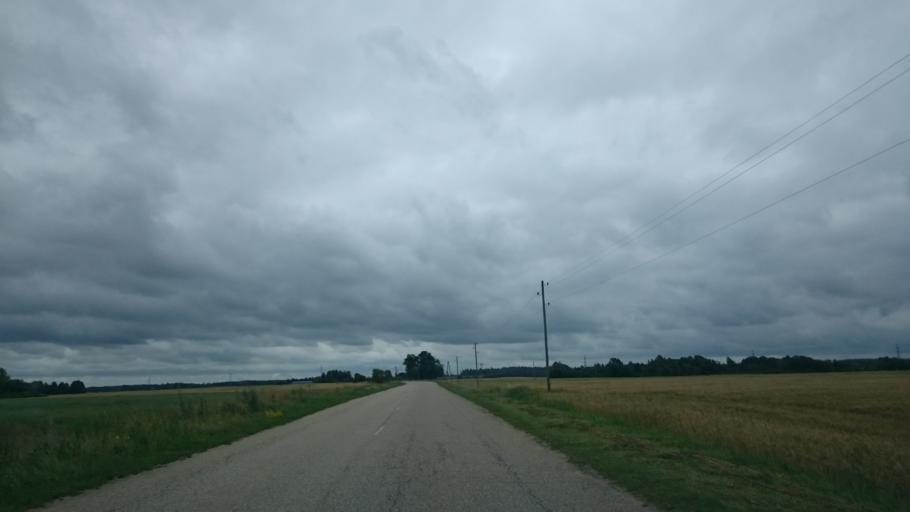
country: LV
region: Durbe
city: Liegi
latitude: 56.7281
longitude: 21.4088
